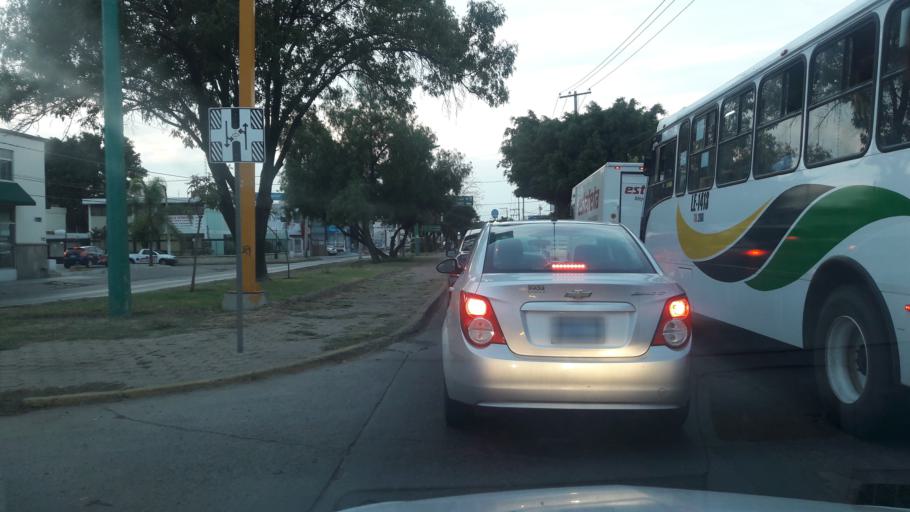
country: MX
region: Guanajuato
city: Leon
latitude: 21.1100
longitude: -101.6690
